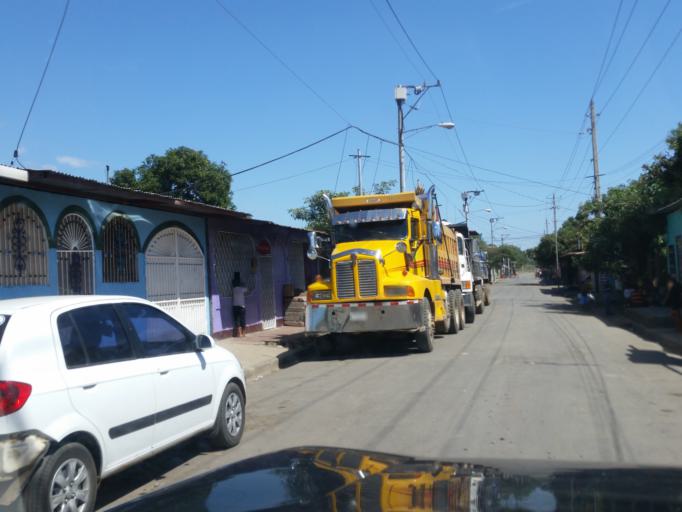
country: NI
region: Managua
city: Managua
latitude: 12.1557
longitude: -86.2686
